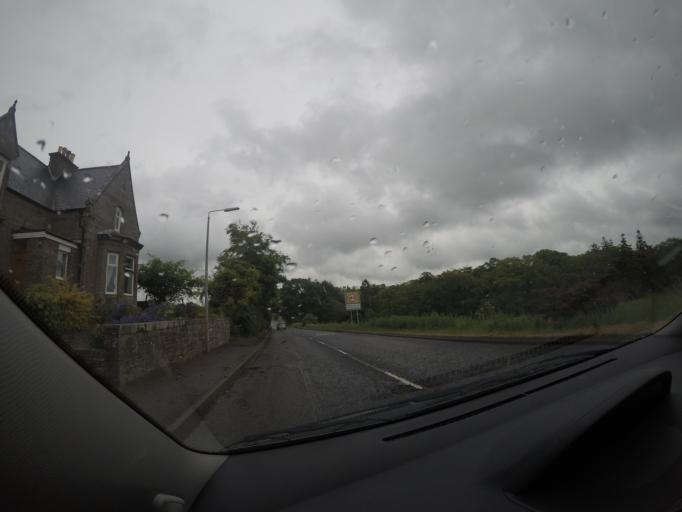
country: GB
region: Scotland
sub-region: Angus
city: Brechin
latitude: 56.7504
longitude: -2.6452
